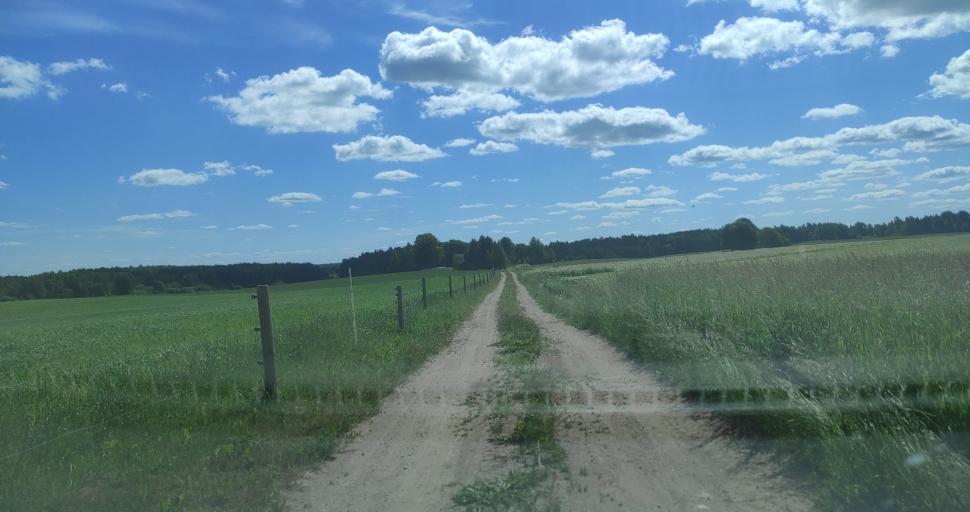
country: LV
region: Alsunga
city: Alsunga
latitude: 56.8976
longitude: 21.7152
